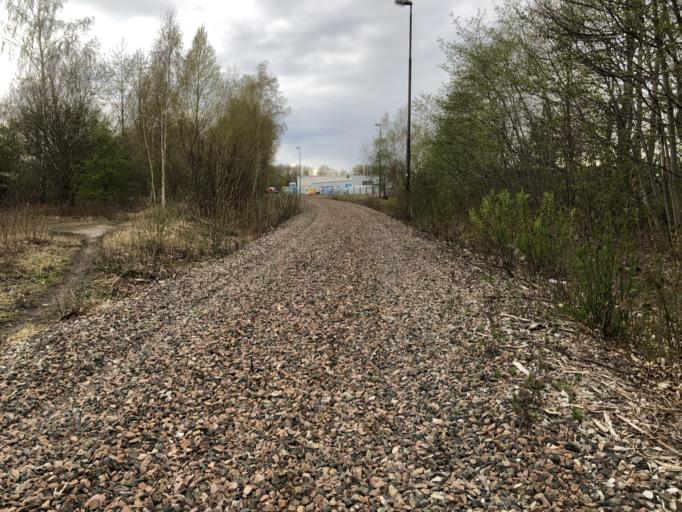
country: SE
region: Skane
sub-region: Malmo
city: Tygelsjo
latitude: 55.5535
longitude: 13.0417
